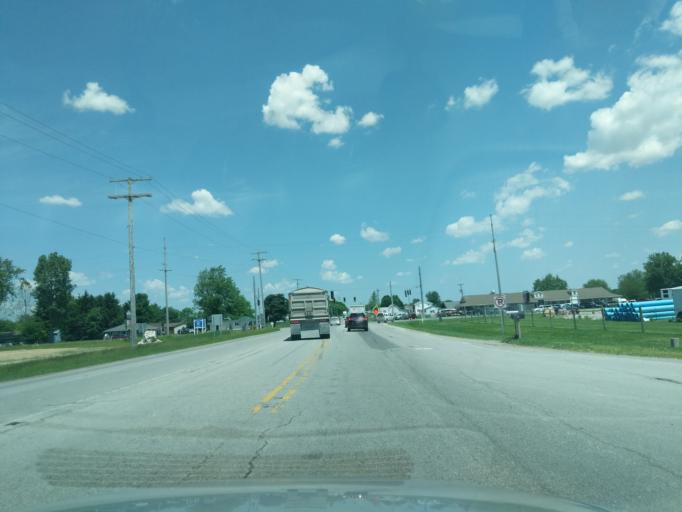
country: US
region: Indiana
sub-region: LaGrange County
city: Topeka
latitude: 41.6534
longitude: -85.5802
